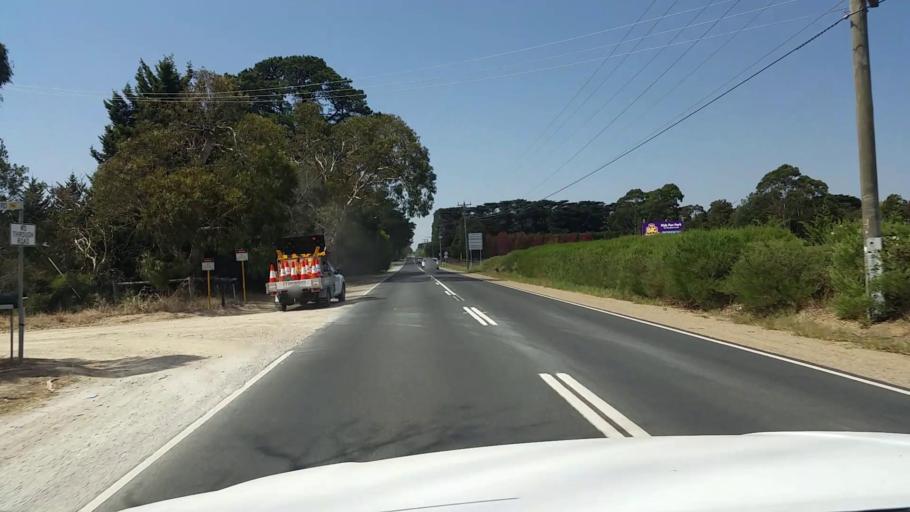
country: AU
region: Victoria
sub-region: Mornington Peninsula
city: Moorooduc
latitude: -38.2566
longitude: 145.1332
